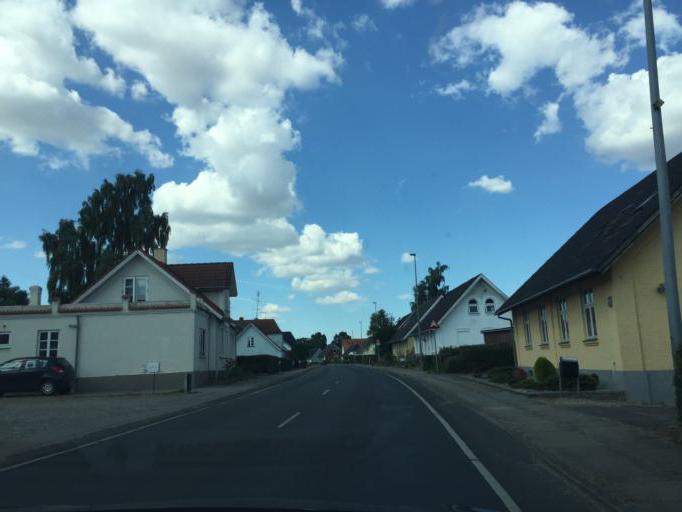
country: DK
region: South Denmark
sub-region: Assens Kommune
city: Harby
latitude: 55.2201
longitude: 10.1209
